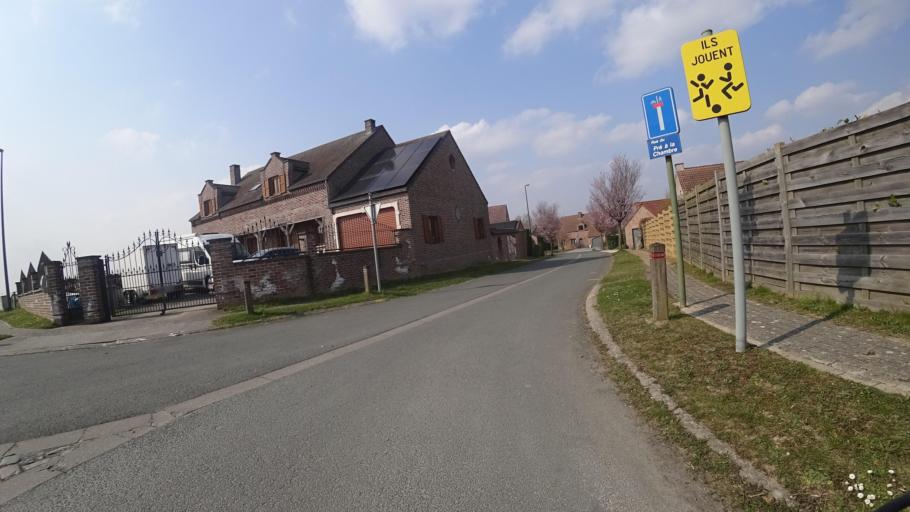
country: BE
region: Wallonia
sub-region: Province du Brabant Wallon
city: Chastre-Villeroux-Blanmont
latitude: 50.6224
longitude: 4.6468
